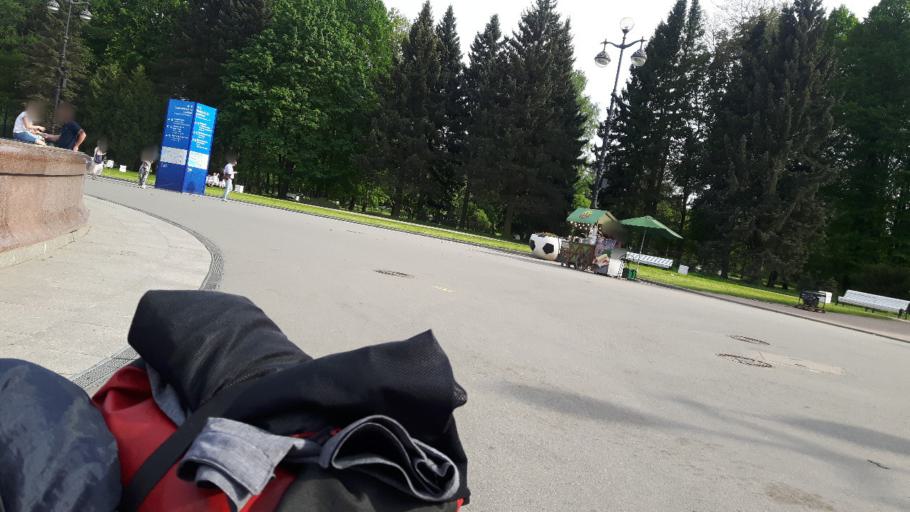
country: RU
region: St.-Petersburg
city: Staraya Derevnya
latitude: 59.9721
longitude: 30.2415
